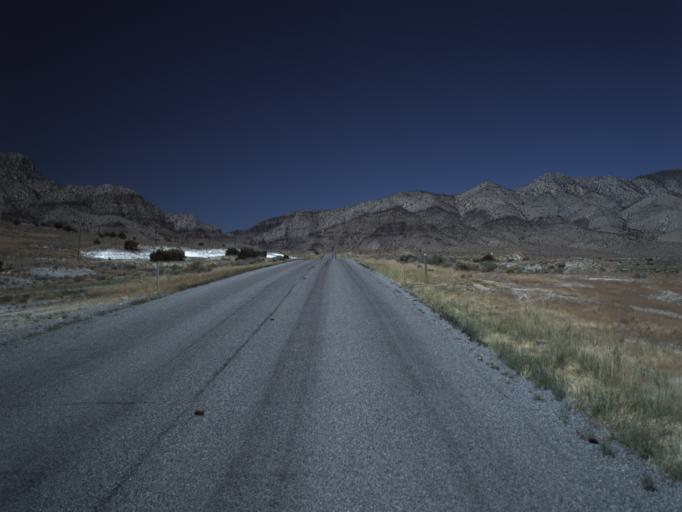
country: US
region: Utah
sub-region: Beaver County
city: Milford
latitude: 39.0853
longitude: -113.5190
